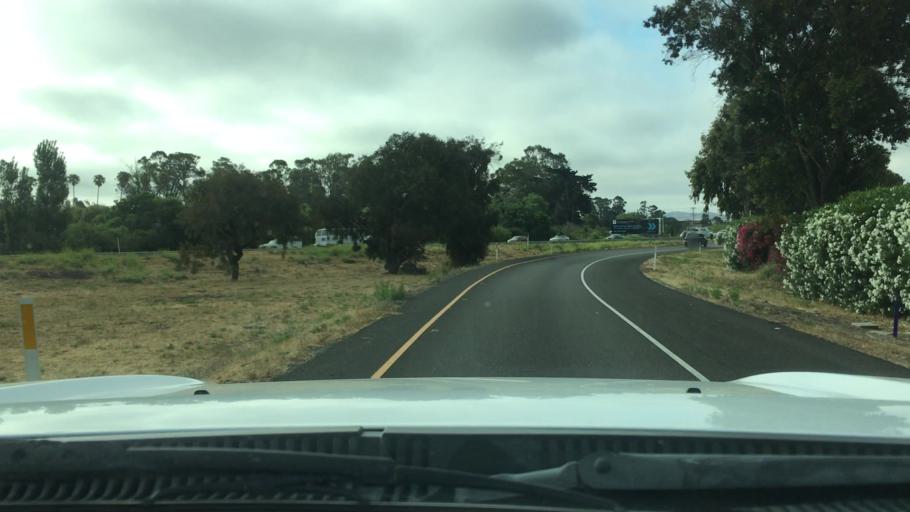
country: US
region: California
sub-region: San Luis Obispo County
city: San Luis Obispo
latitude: 35.2634
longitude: -120.6746
